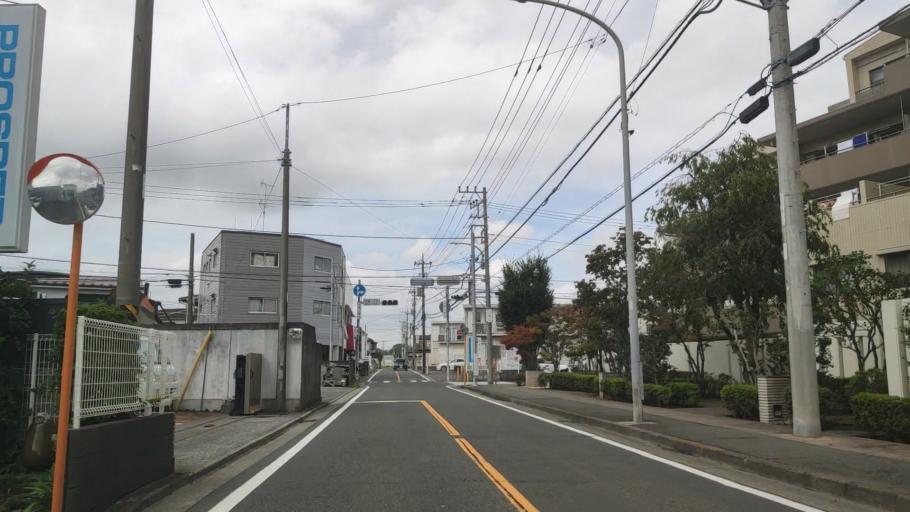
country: JP
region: Kanagawa
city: Minami-rinkan
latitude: 35.4780
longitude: 139.4756
